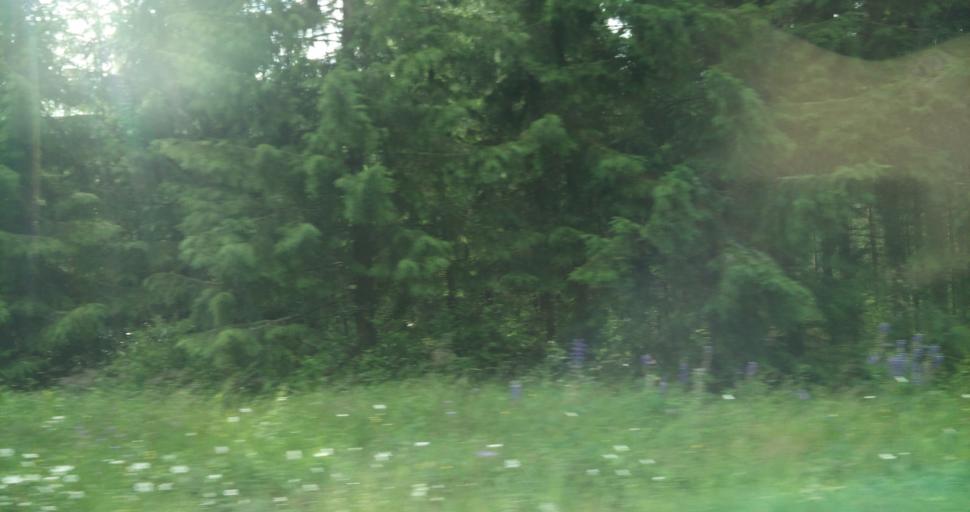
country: SE
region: Vaermland
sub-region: Hagfors Kommun
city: Ekshaerad
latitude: 60.0308
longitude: 13.4854
